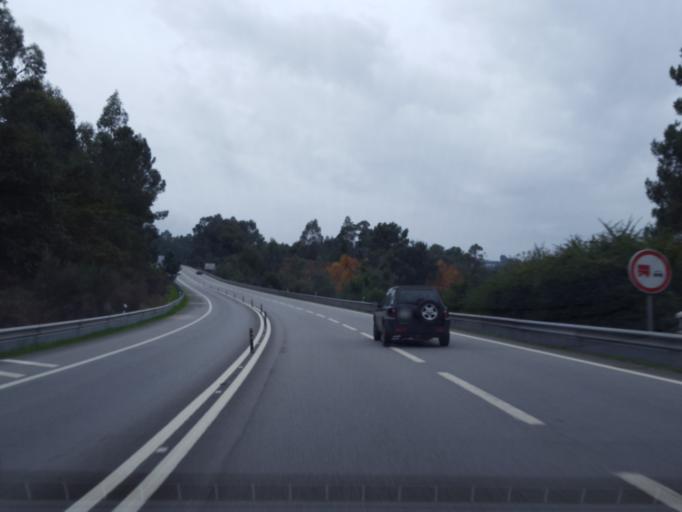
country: PT
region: Porto
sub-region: Marco de Canaveses
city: Marco de Canavezes
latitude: 41.2270
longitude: -8.1927
